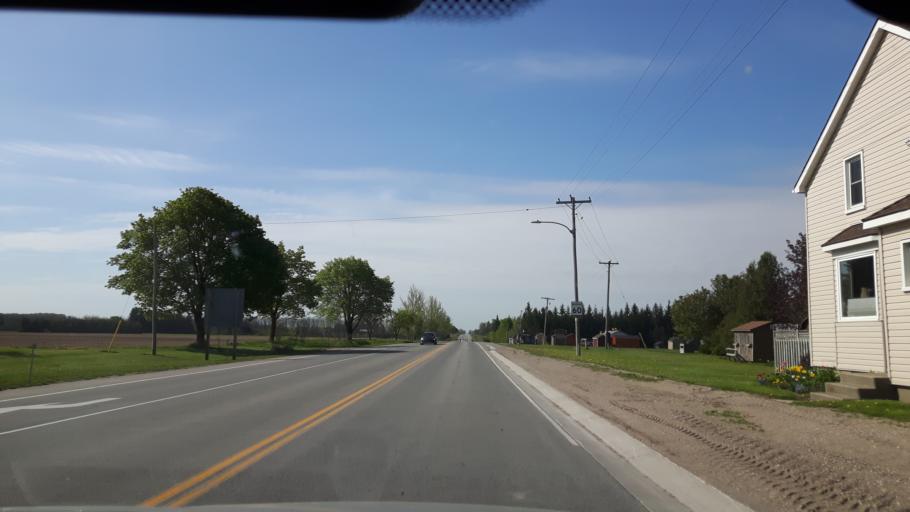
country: CA
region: Ontario
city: Bluewater
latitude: 43.4708
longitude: -81.5060
